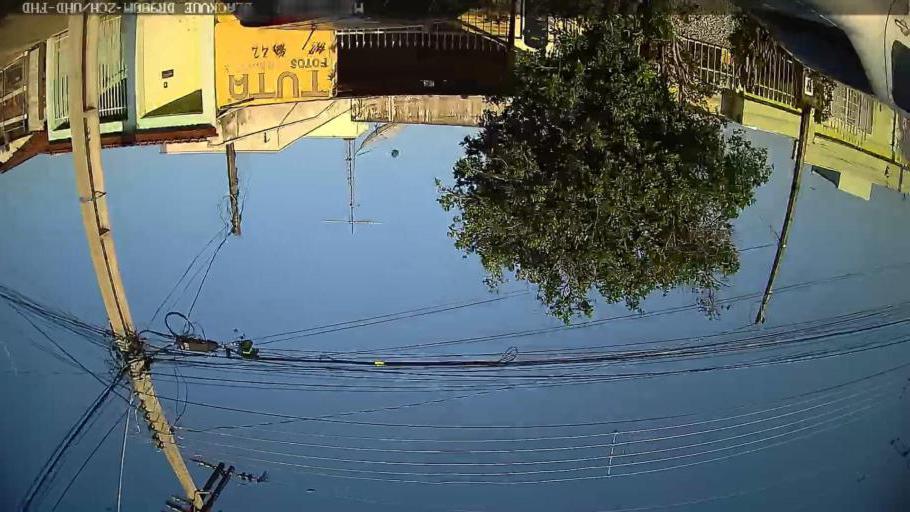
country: BR
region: Sao Paulo
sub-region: Itupeva
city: Itupeva
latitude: -23.2473
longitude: -47.0531
